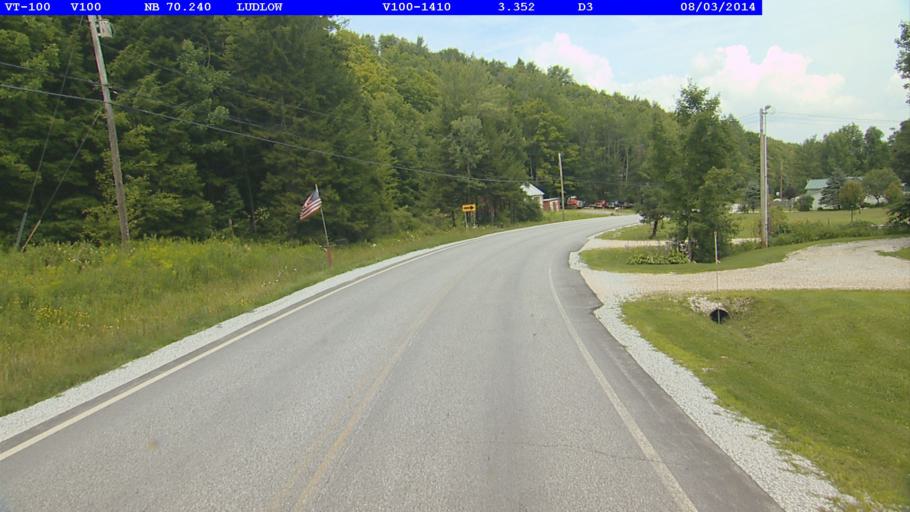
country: US
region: Vermont
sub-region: Windsor County
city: Chester
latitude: 43.3754
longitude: -72.7185
